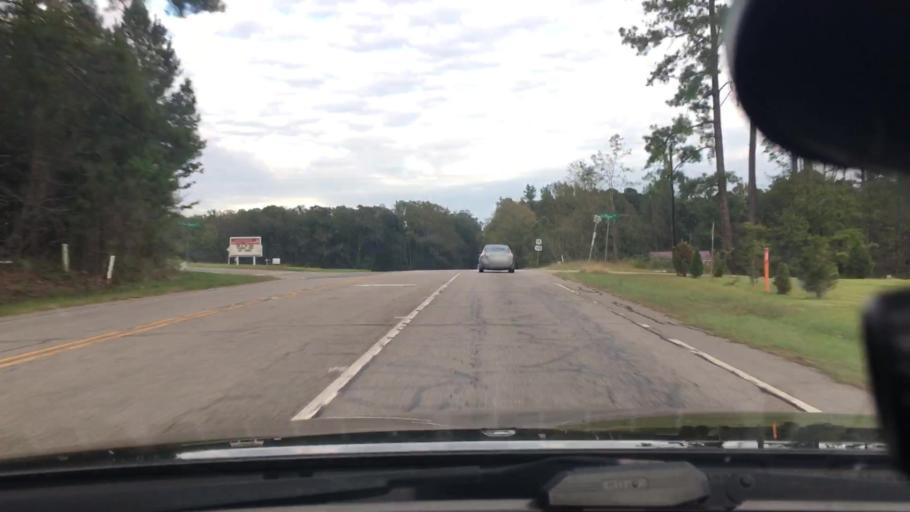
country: US
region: North Carolina
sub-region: Moore County
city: Carthage
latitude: 35.3560
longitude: -79.3414
